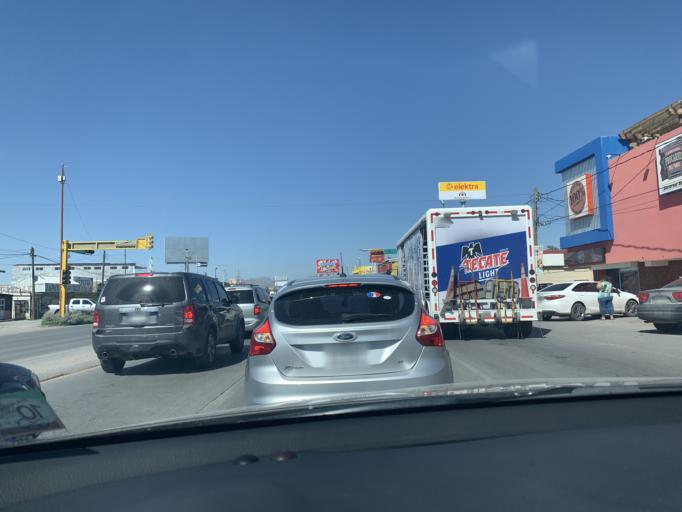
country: US
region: Texas
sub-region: El Paso County
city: Socorro
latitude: 31.6841
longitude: -106.3730
